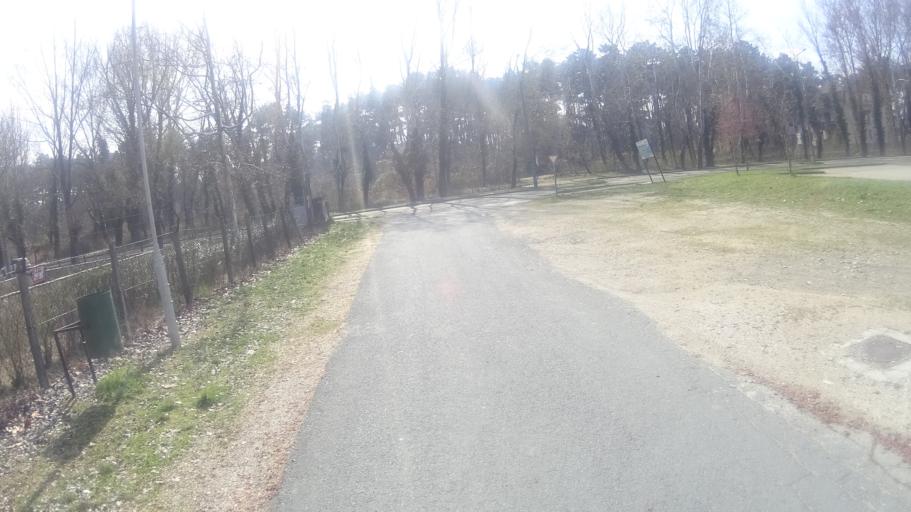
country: HU
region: Somogy
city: Balatonszabadi
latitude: 46.9270
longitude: 18.1014
